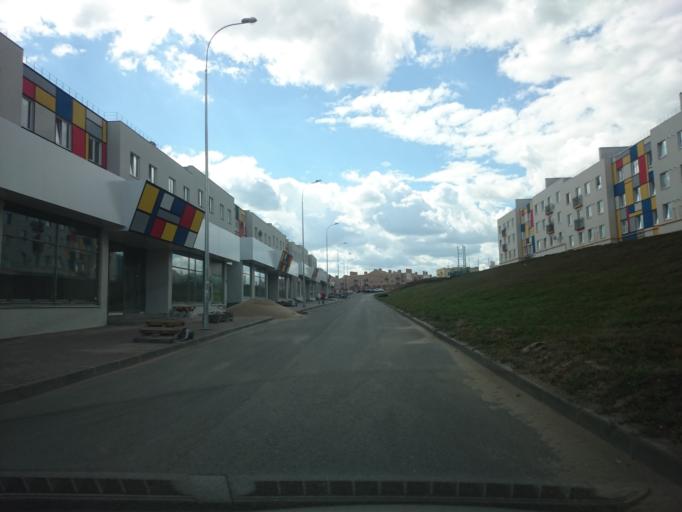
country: RU
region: Samara
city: Petra-Dubrava
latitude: 53.3235
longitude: 50.3148
